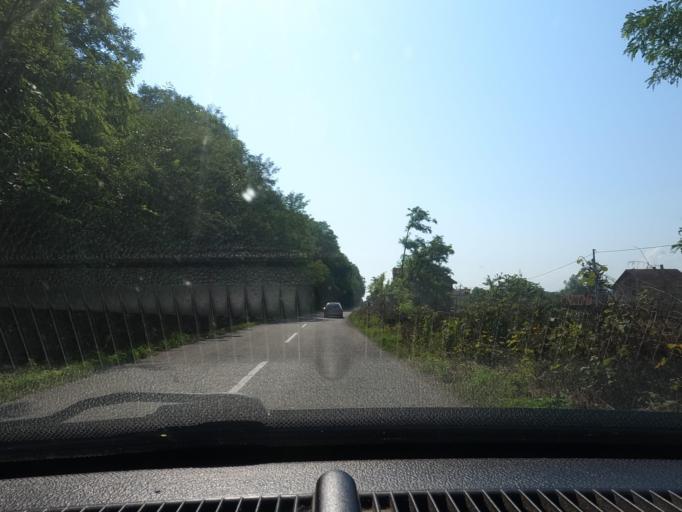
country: RS
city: Kozjak
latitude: 44.5553
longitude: 19.3208
